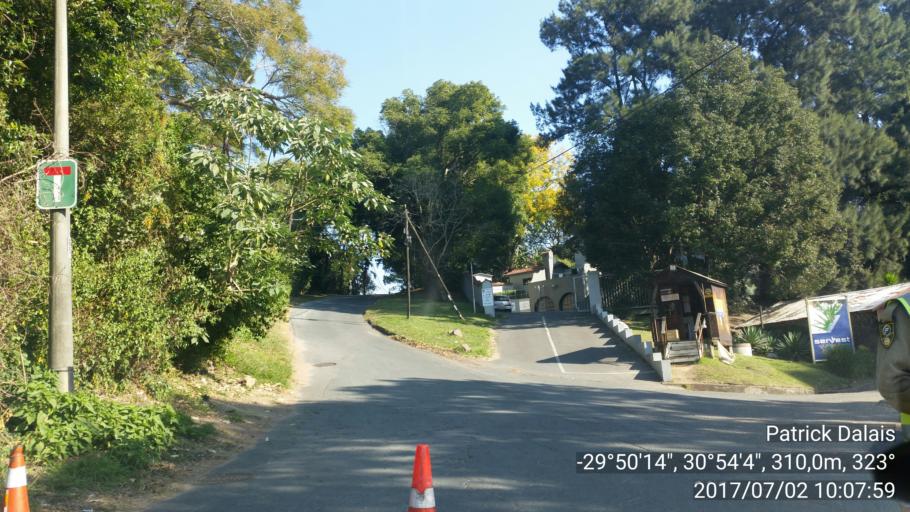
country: ZA
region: KwaZulu-Natal
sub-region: eThekwini Metropolitan Municipality
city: Berea
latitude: -29.8375
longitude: 30.9013
